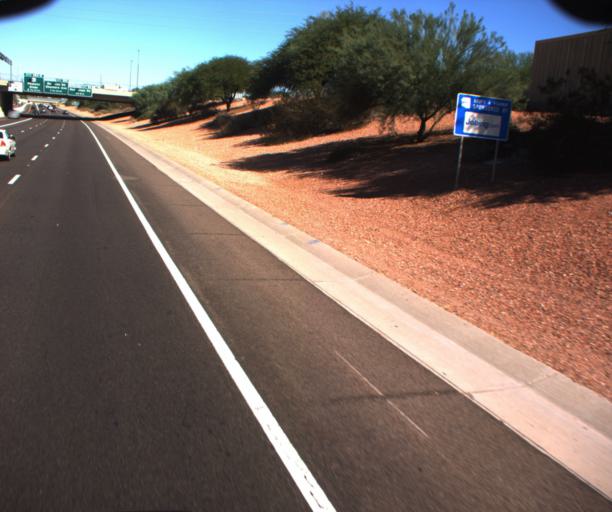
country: US
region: Arizona
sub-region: Maricopa County
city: San Carlos
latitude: 33.3478
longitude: -111.8935
